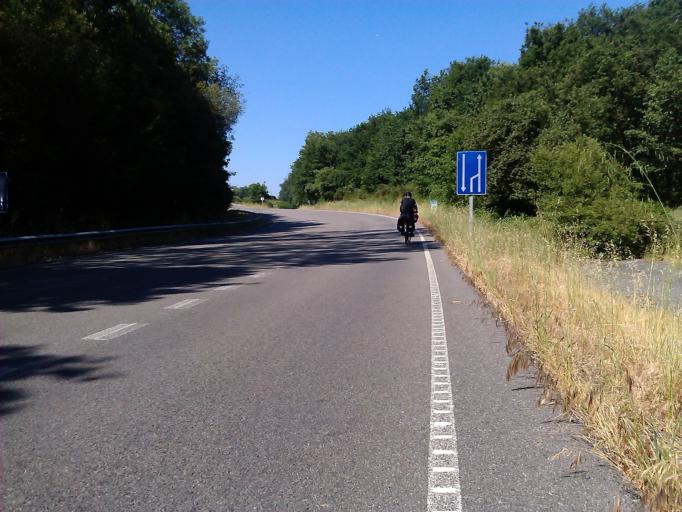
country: ES
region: Galicia
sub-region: Provincia de Lugo
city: Sarria
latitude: 42.7615
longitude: -7.3909
